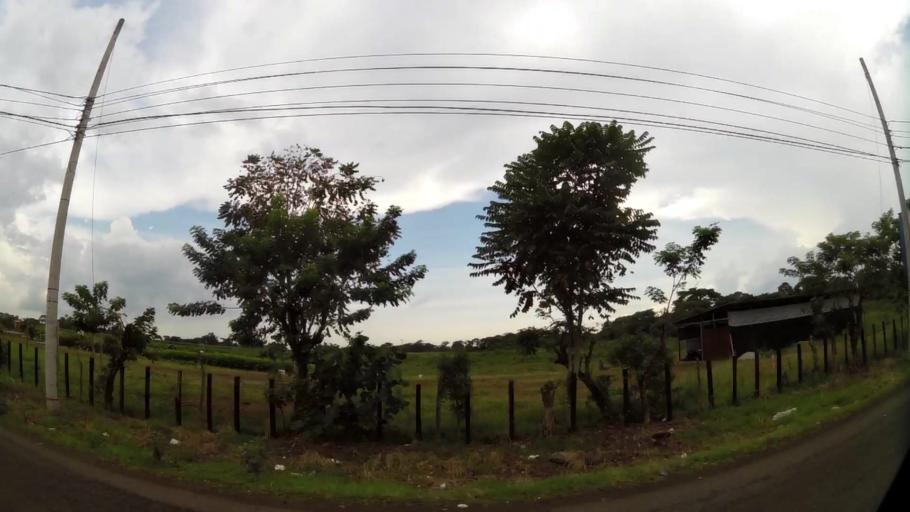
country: PA
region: Panama
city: Cabra Numero Uno
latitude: 9.1134
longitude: -79.3544
